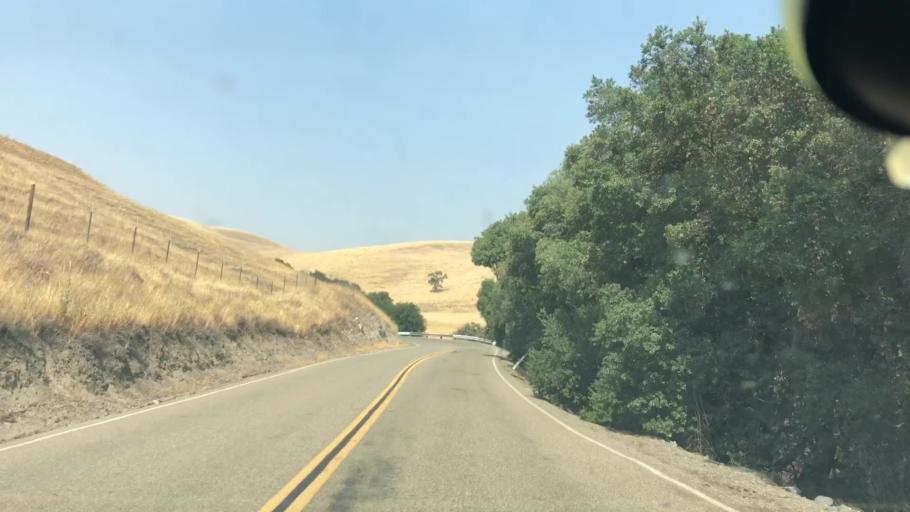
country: US
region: California
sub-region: San Joaquin County
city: Mountain House
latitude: 37.6496
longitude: -121.6159
